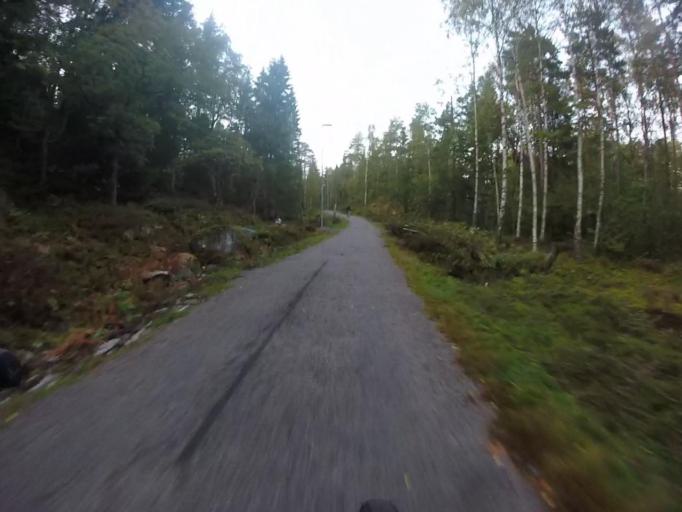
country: SE
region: Vaestra Goetaland
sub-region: Trollhattan
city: Trollhattan
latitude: 58.2943
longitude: 12.2697
